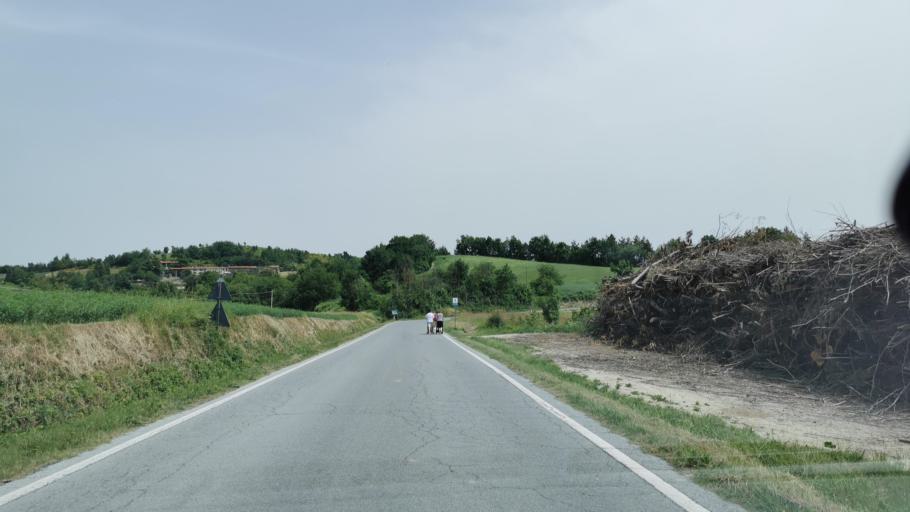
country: IT
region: Piedmont
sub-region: Provincia di Cuneo
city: Sale San Giovanni
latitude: 44.4049
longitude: 8.0756
